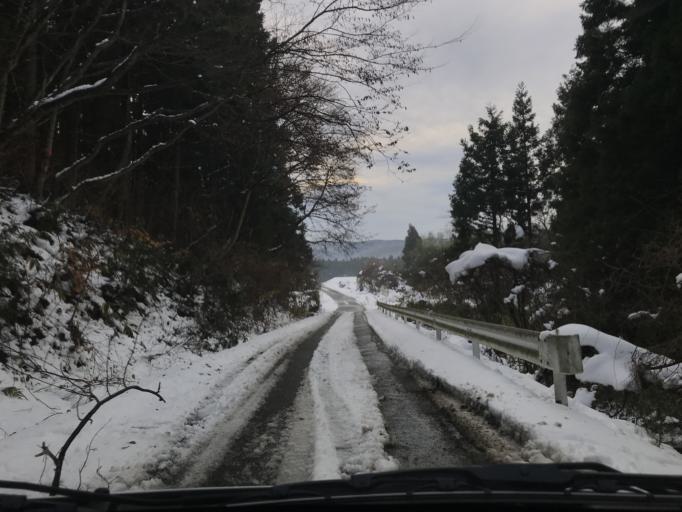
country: JP
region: Iwate
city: Mizusawa
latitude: 39.0512
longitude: 141.0579
